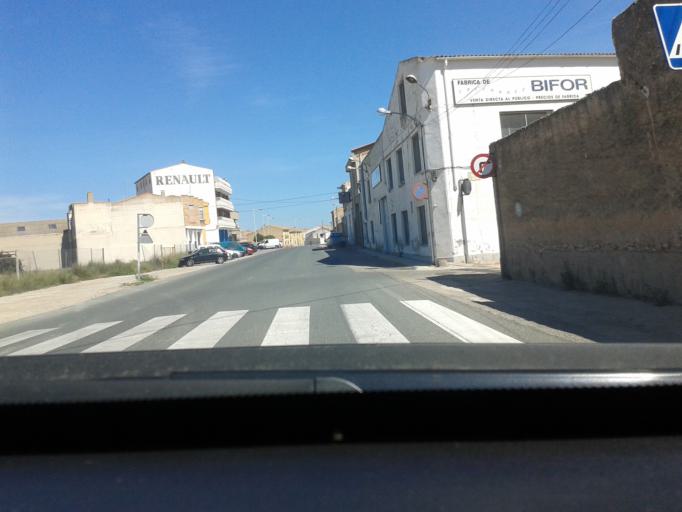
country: ES
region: Castille-La Mancha
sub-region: Provincia de Albacete
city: Caudete
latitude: 38.7076
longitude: -0.9900
